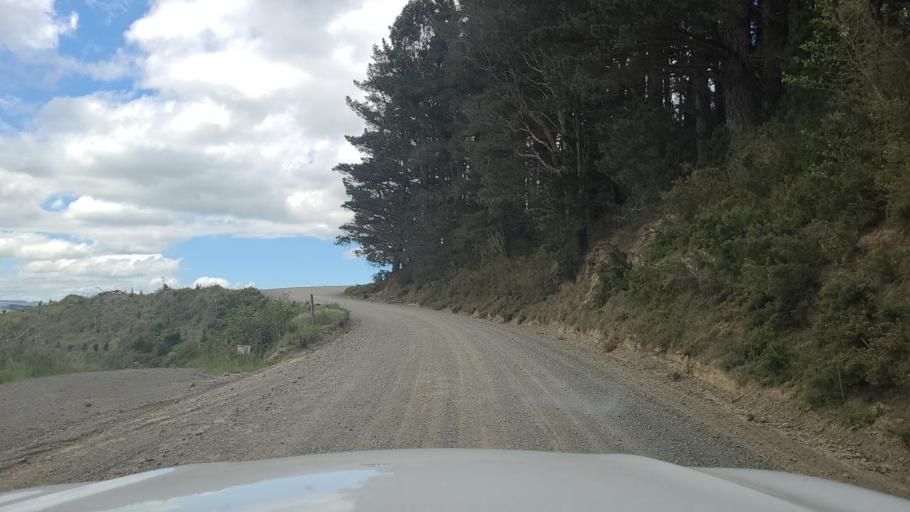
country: NZ
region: Hawke's Bay
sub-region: Napier City
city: Napier
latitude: -39.2486
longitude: 176.7250
